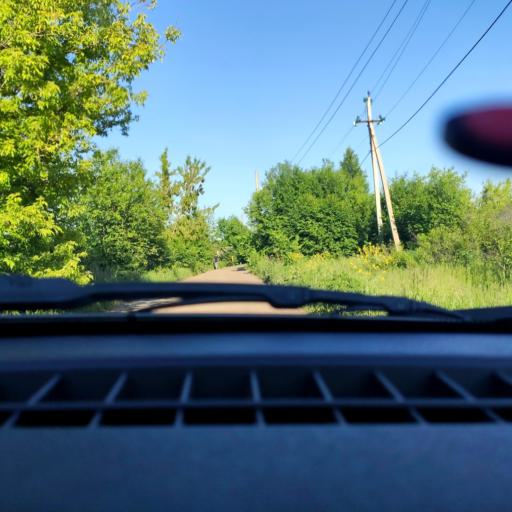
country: RU
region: Bashkortostan
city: Avdon
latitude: 54.4654
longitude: 55.8210
